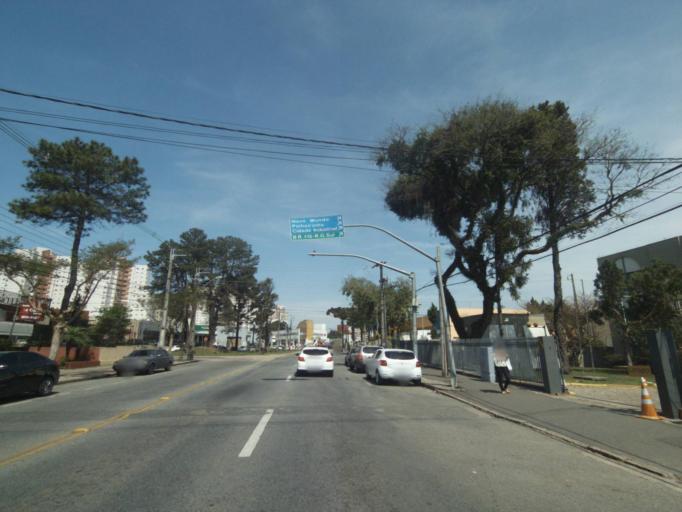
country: BR
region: Parana
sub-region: Curitiba
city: Curitiba
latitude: -25.4692
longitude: -49.2962
